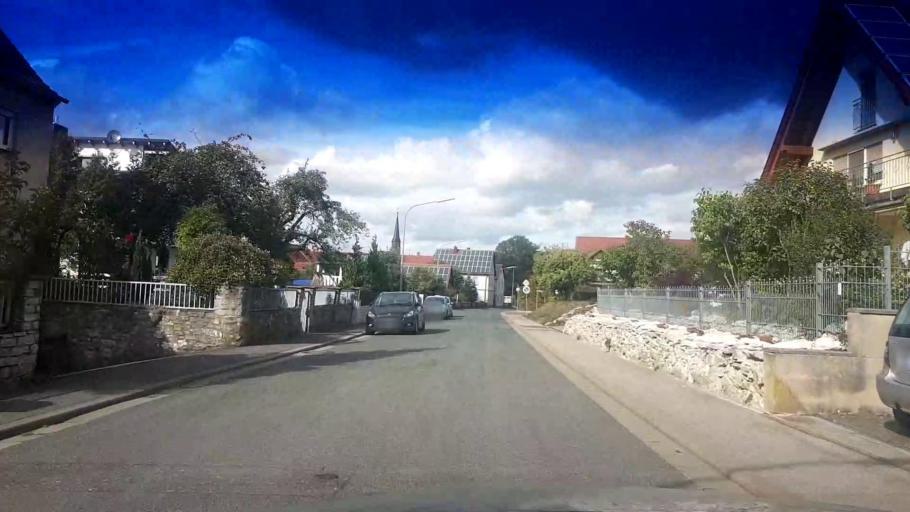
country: DE
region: Bavaria
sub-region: Upper Franconia
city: Schesslitz
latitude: 49.9734
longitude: 11.0319
